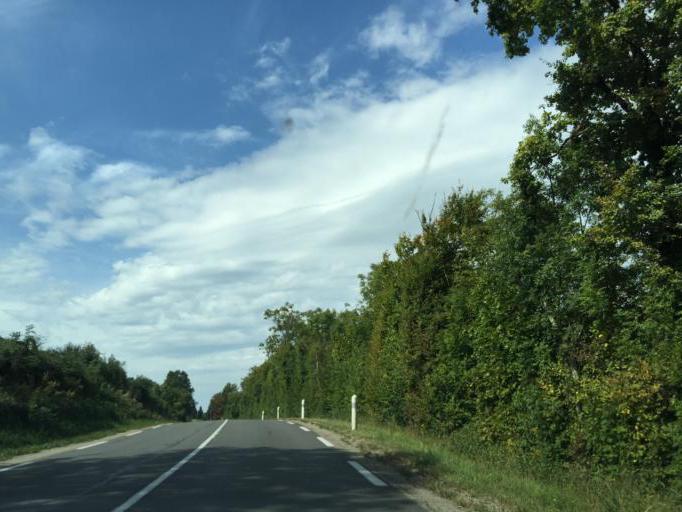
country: FR
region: Rhone-Alpes
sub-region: Departement de l'Isere
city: Saint-Andre-le-Gaz
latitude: 45.5463
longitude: 5.5165
